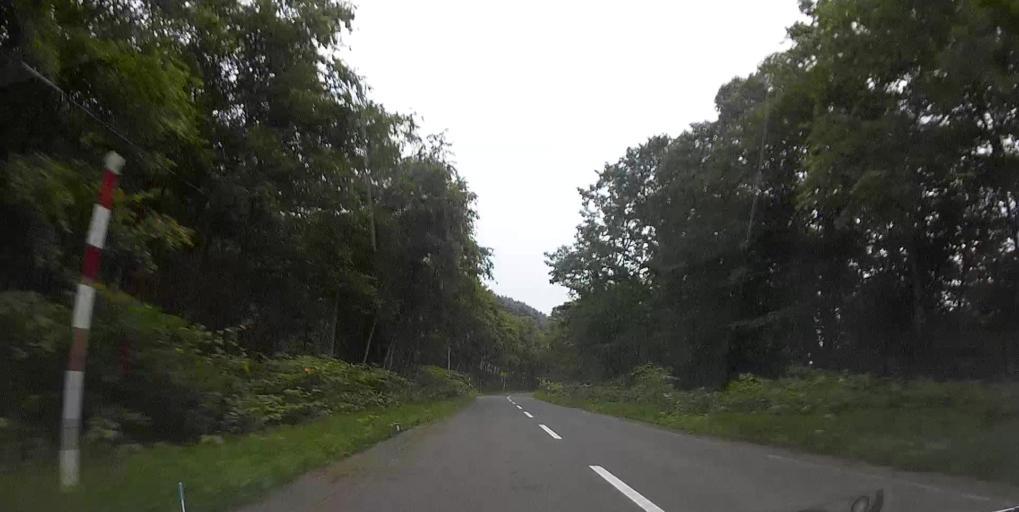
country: JP
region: Hokkaido
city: Nanae
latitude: 42.2737
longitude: 140.0854
